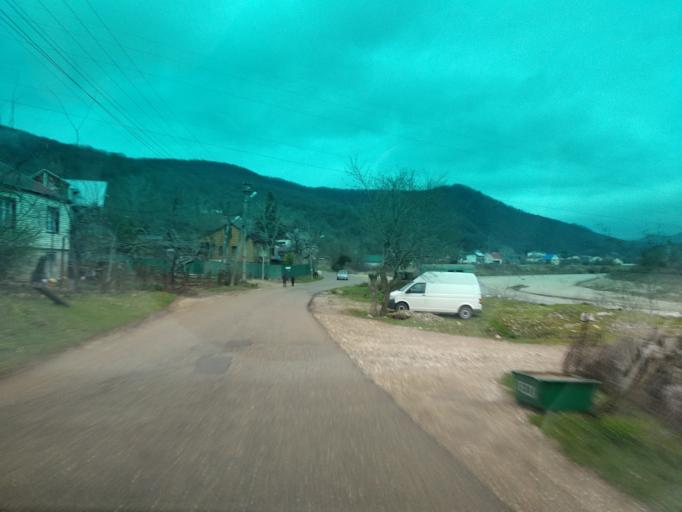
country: RU
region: Krasnodarskiy
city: Novomikhaylovskiy
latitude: 44.2567
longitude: 38.8511
